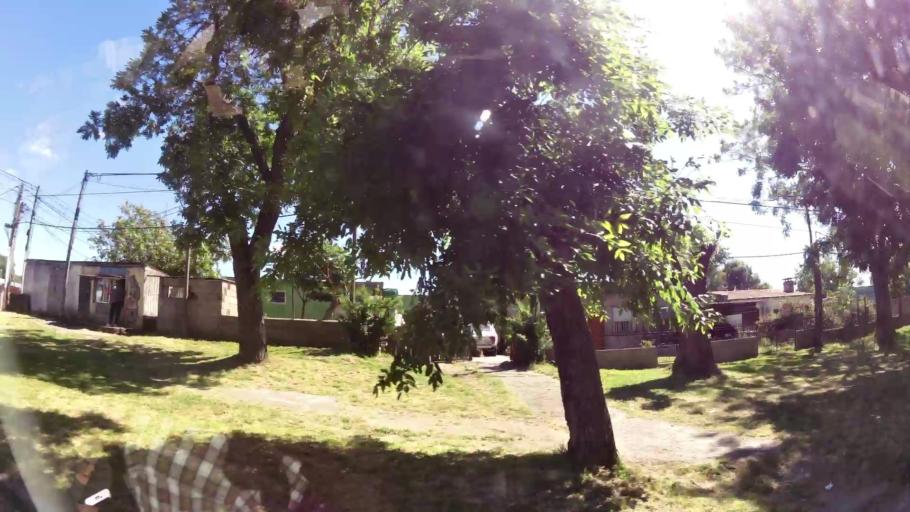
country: UY
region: Canelones
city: Paso de Carrasco
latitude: -34.8451
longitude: -56.1165
